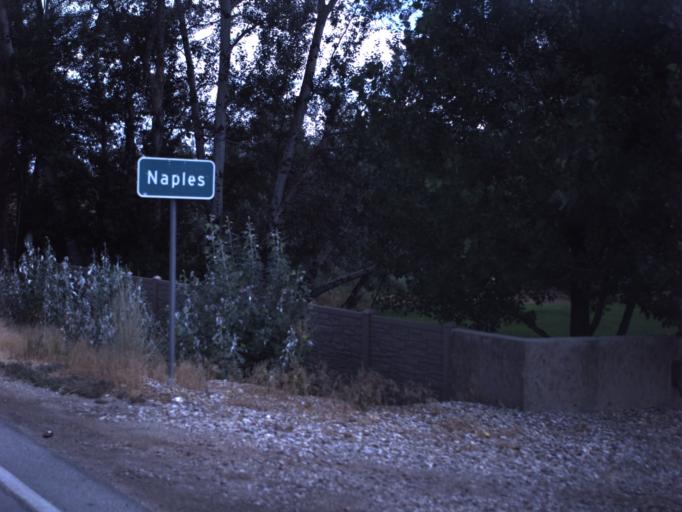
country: US
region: Utah
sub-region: Uintah County
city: Naples
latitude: 40.4118
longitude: -109.4991
